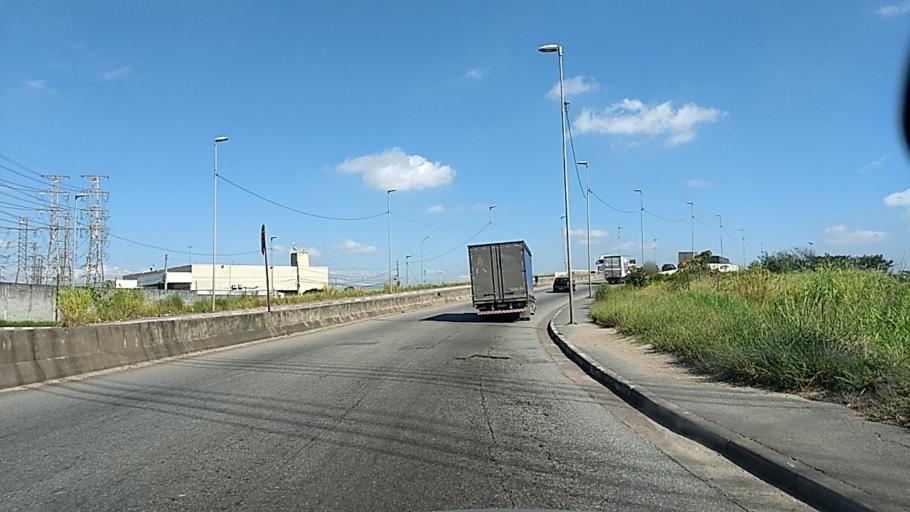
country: BR
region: Sao Paulo
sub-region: Guarulhos
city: Guarulhos
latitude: -23.4861
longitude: -46.5583
